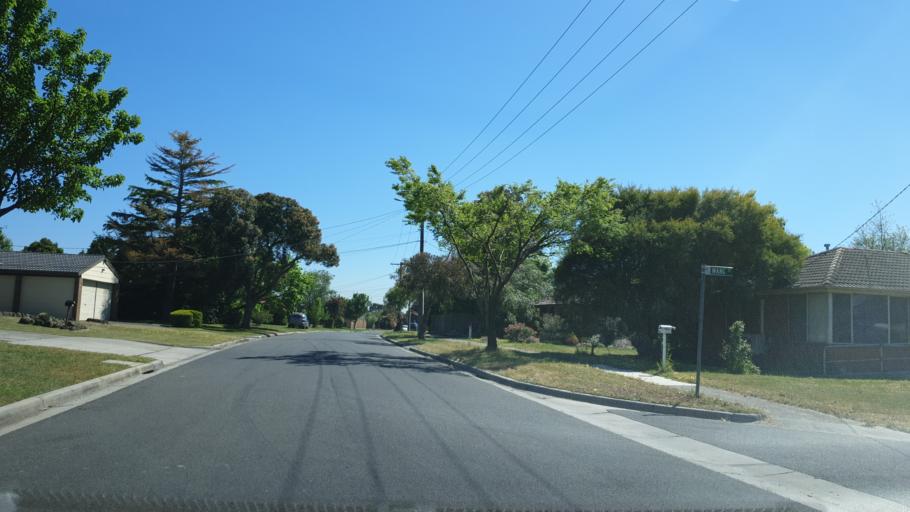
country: AU
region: Victoria
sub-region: Casey
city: Cranbourne
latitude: -38.1024
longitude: 145.2764
